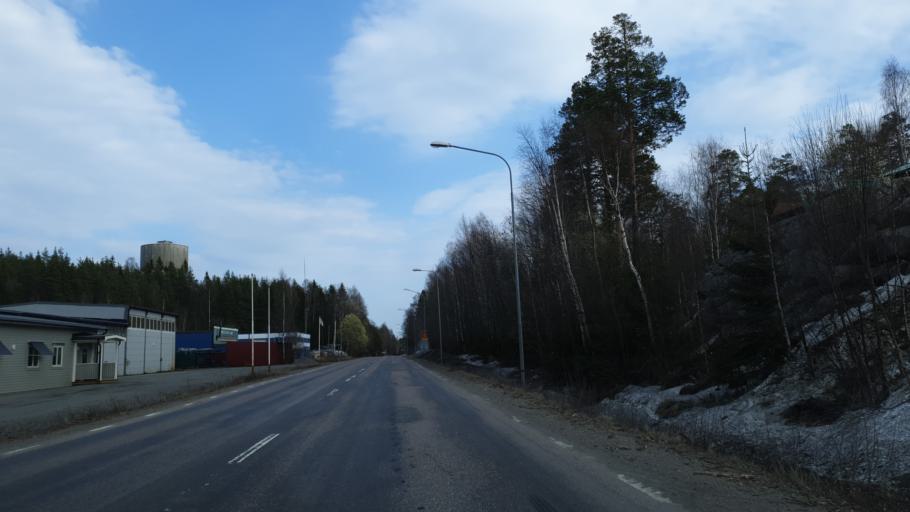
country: SE
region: Gaevleborg
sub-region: Hudiksvalls Kommun
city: Iggesund
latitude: 61.6443
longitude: 17.0570
